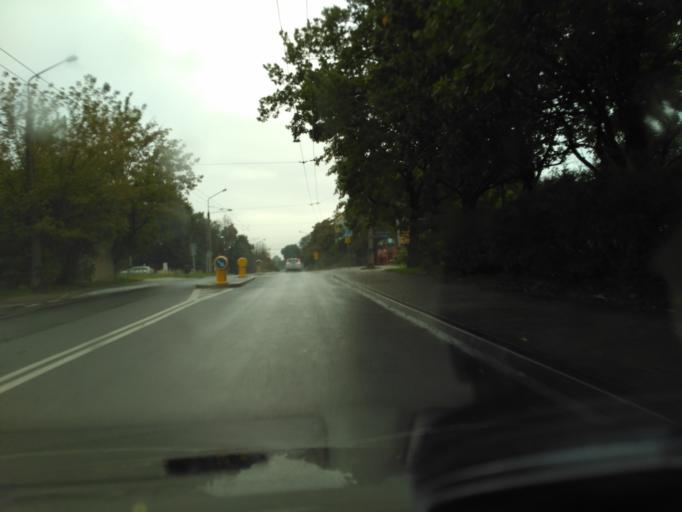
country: PL
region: Lublin Voivodeship
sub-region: Powiat lubelski
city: Lublin
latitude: 51.2463
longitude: 22.6017
